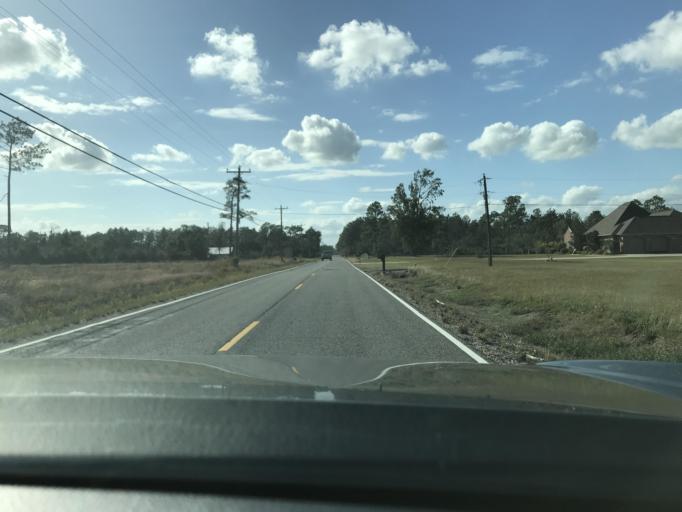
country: US
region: Louisiana
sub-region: Calcasieu Parish
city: Moss Bluff
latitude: 30.3226
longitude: -93.2651
